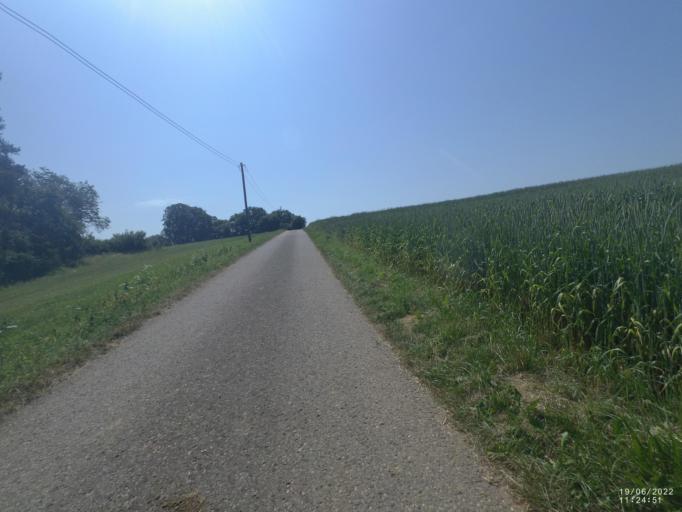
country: DE
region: Baden-Wuerttemberg
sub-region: Tuebingen Region
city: Weidenstetten
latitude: 48.6080
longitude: 9.9798
